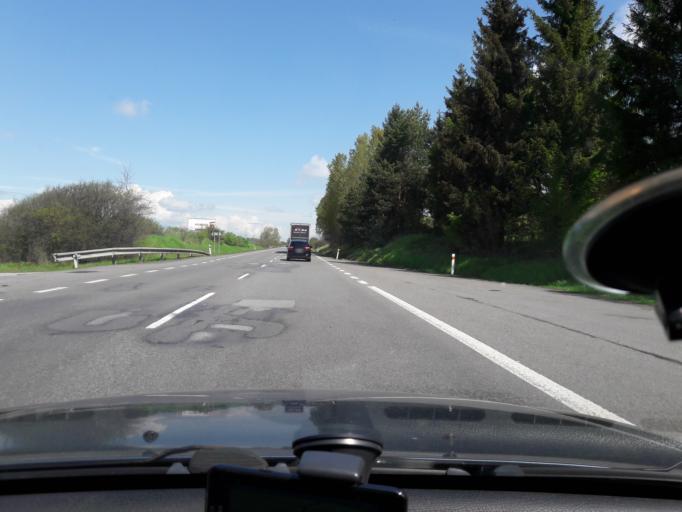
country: SK
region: Banskobystricky
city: Krupina
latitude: 48.4330
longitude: 19.0955
